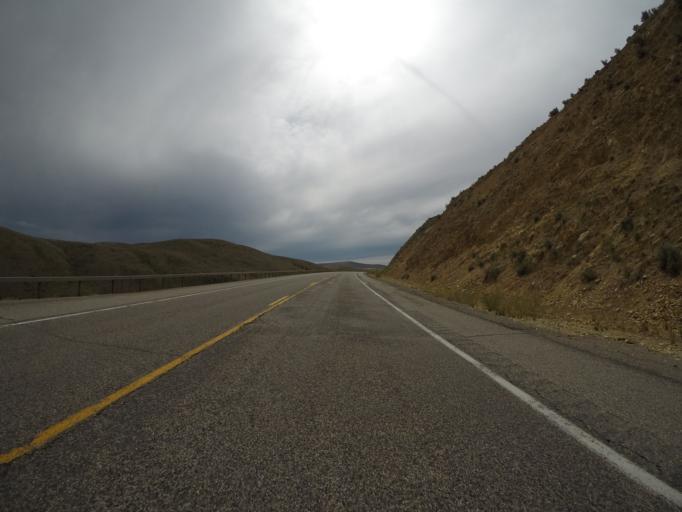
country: US
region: Wyoming
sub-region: Lincoln County
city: Kemmerer
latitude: 41.8239
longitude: -110.8561
